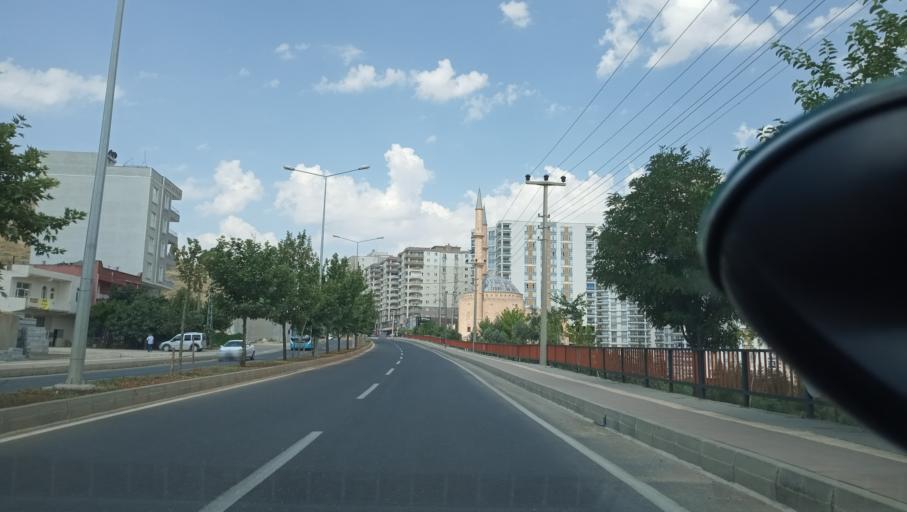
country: TR
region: Mardin
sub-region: Mardin Ilcesi
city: Mardin
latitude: 37.3221
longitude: 40.7346
